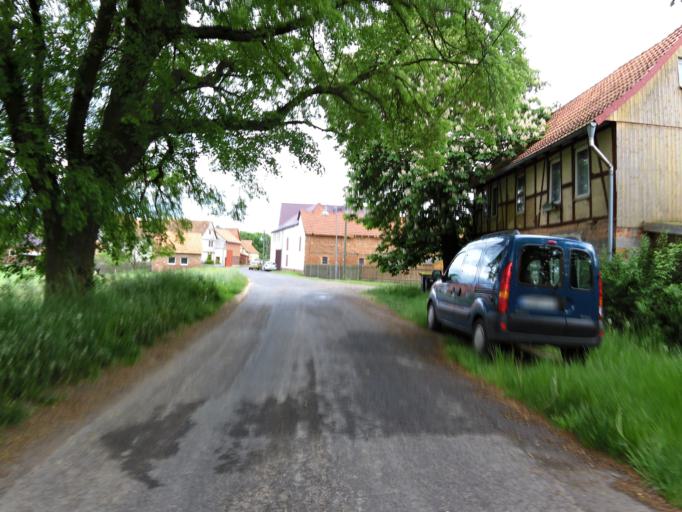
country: DE
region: Thuringia
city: Dippach
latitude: 50.9248
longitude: 10.0832
